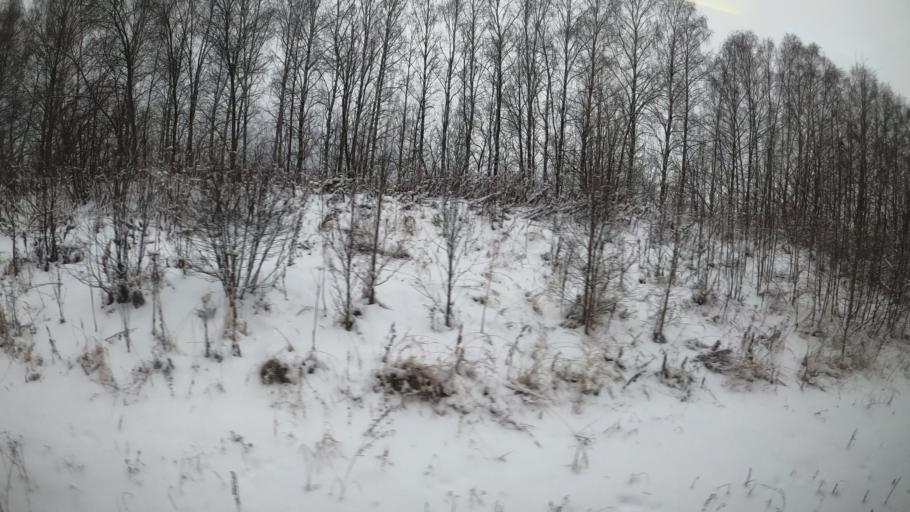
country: RU
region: Jaroslavl
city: Pereslavl'-Zalesskiy
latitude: 56.6869
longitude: 38.9193
